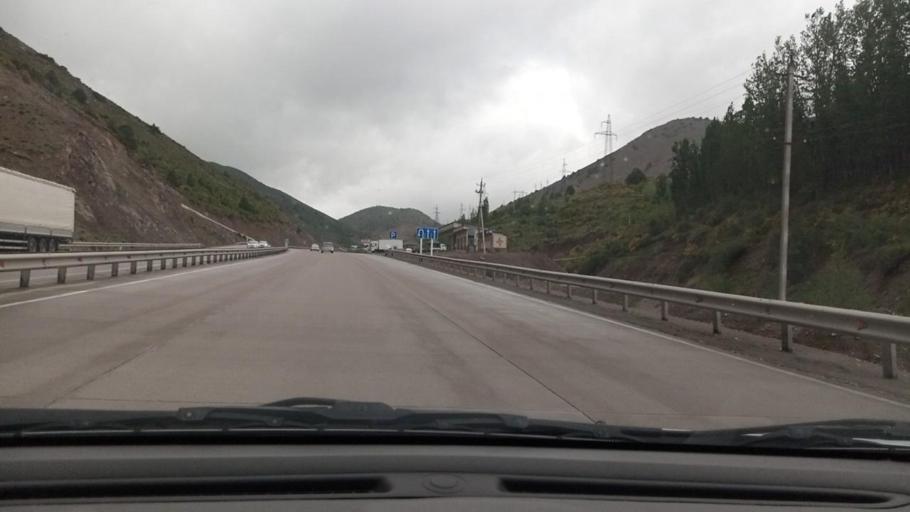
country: UZ
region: Toshkent
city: Angren
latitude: 41.0492
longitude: 70.5696
